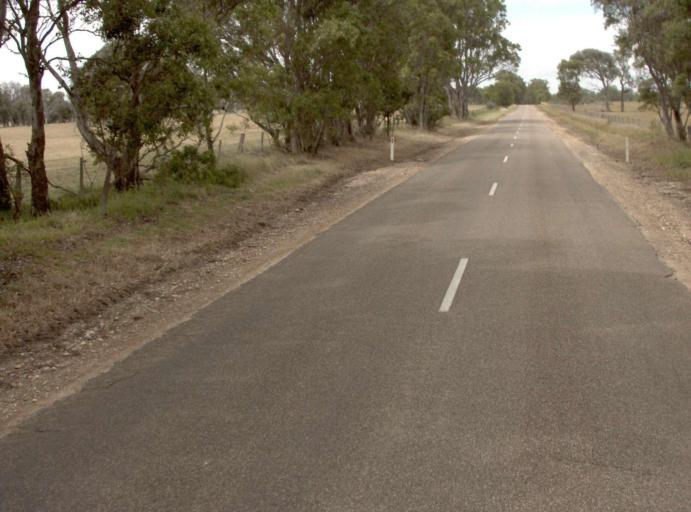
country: AU
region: Victoria
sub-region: Wellington
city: Sale
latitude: -37.8754
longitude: 147.0663
